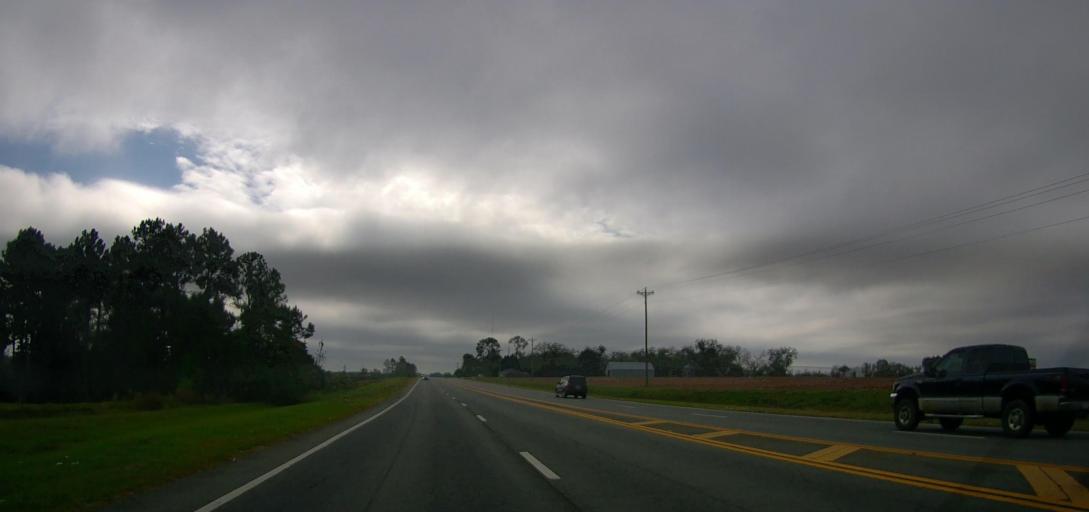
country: US
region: Georgia
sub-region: Tift County
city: Omega
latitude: 31.3631
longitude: -83.5765
